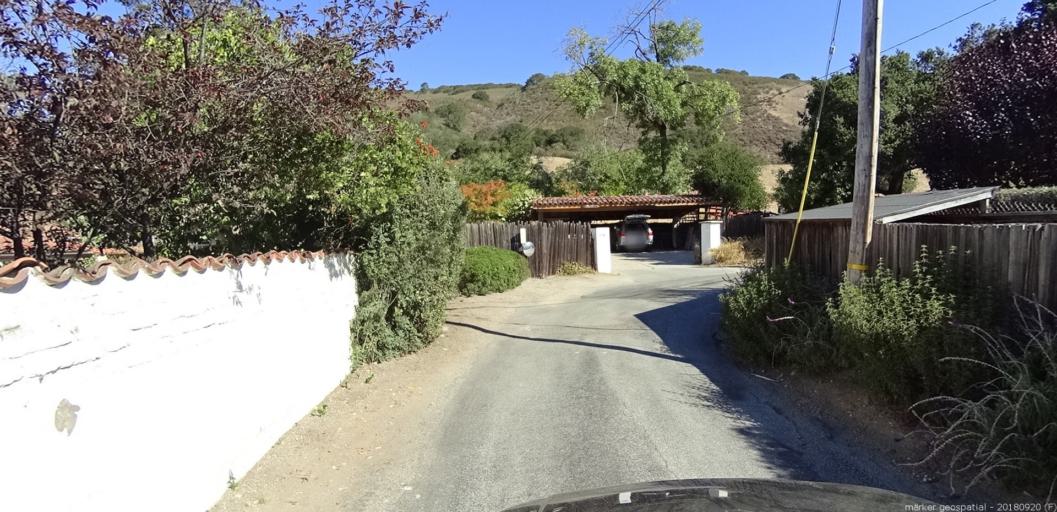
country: US
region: California
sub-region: Monterey County
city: Del Rey Oaks
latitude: 36.5321
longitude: -121.8298
